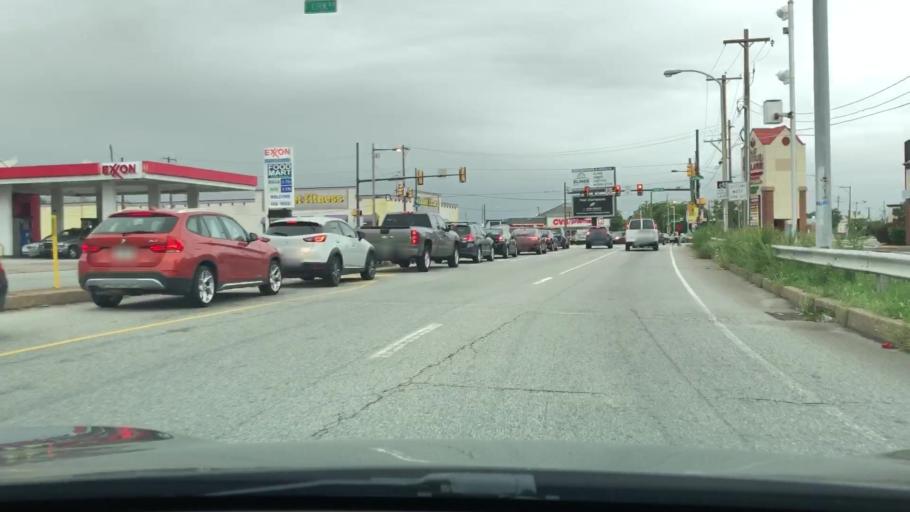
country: US
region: Pennsylvania
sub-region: Philadelphia County
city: Philadelphia
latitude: 39.9747
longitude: -75.1216
